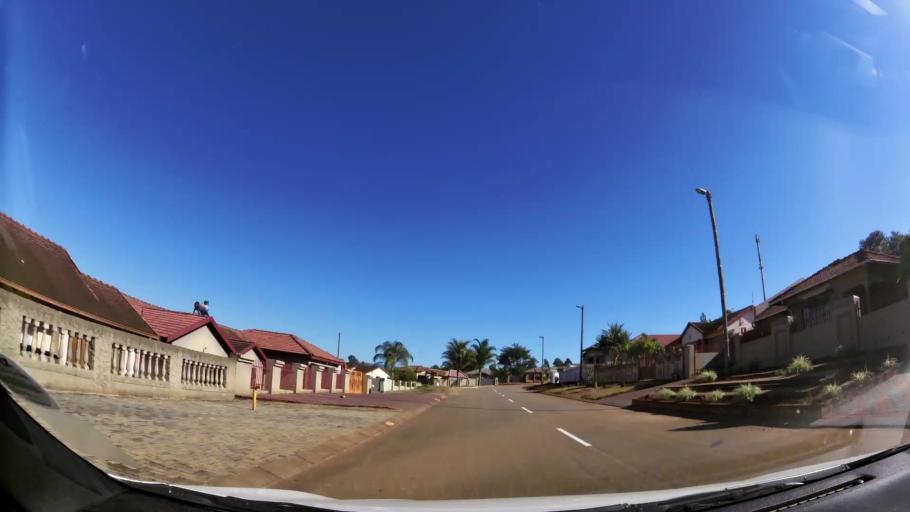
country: ZA
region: Limpopo
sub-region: Mopani District Municipality
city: Tzaneen
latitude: -23.8475
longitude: 30.1638
